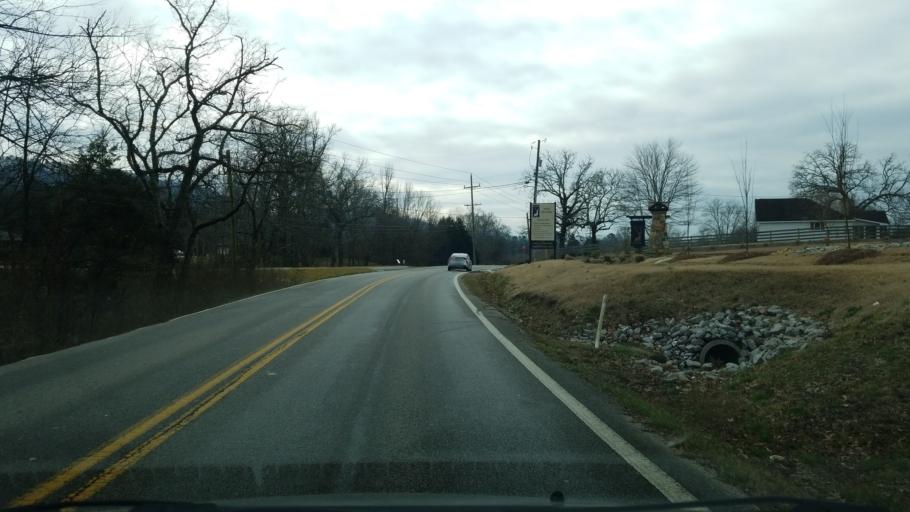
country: US
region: Tennessee
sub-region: Hamilton County
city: Collegedale
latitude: 35.0249
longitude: -85.0853
